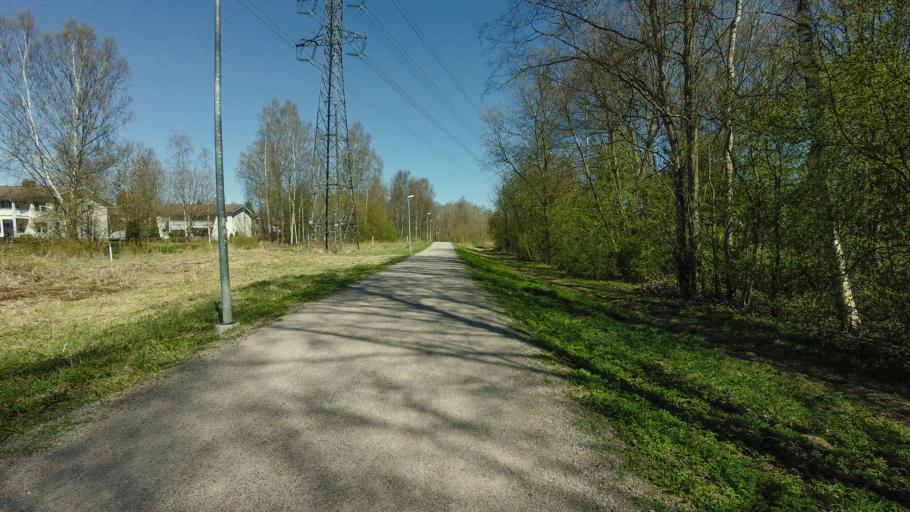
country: FI
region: Uusimaa
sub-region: Helsinki
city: Vantaa
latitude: 60.2268
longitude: 25.0934
